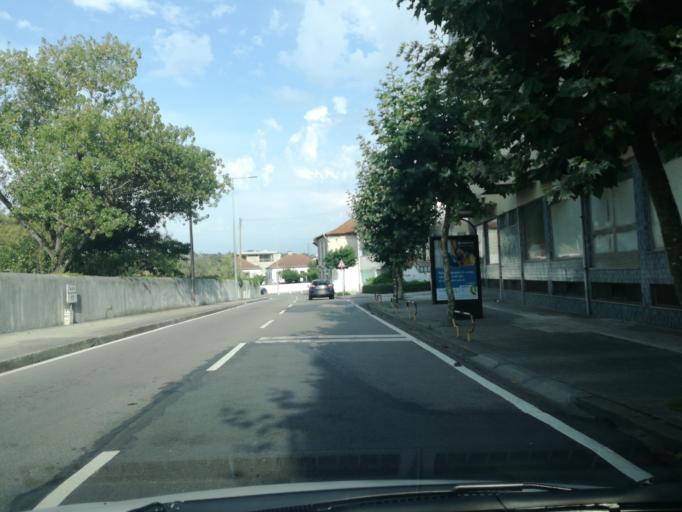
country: PT
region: Aveiro
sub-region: Espinho
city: Espinho
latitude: 41.0122
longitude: -8.6367
